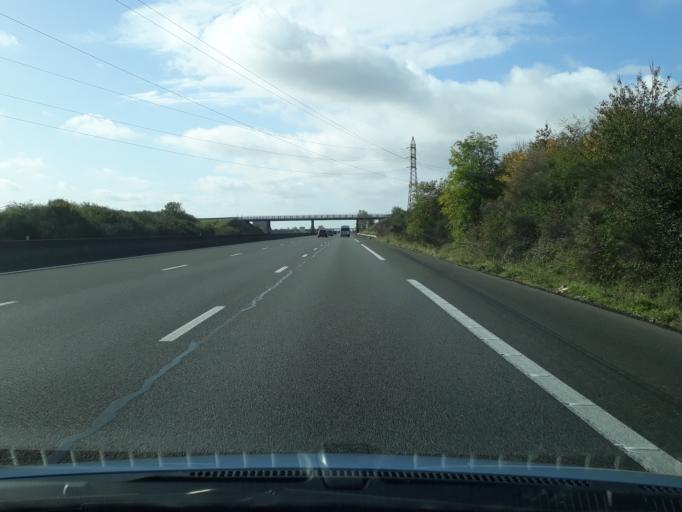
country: FR
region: Centre
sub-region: Departement du Loiret
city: Beaugency
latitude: 47.7943
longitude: 1.6077
